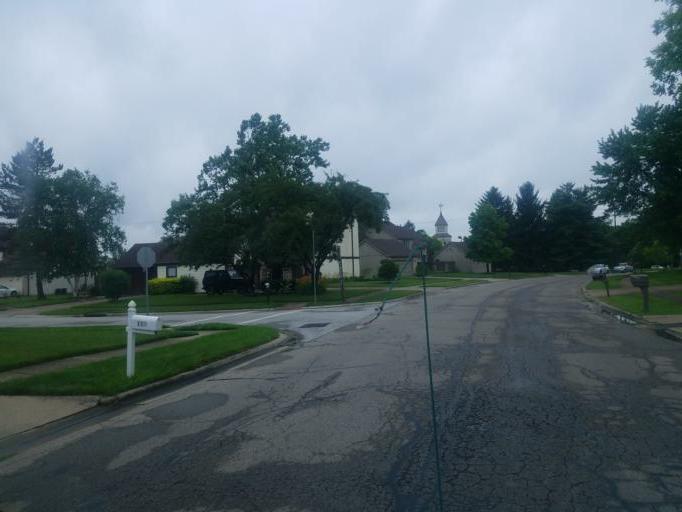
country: US
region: Ohio
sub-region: Franklin County
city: Gahanna
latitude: 40.0161
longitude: -82.8515
